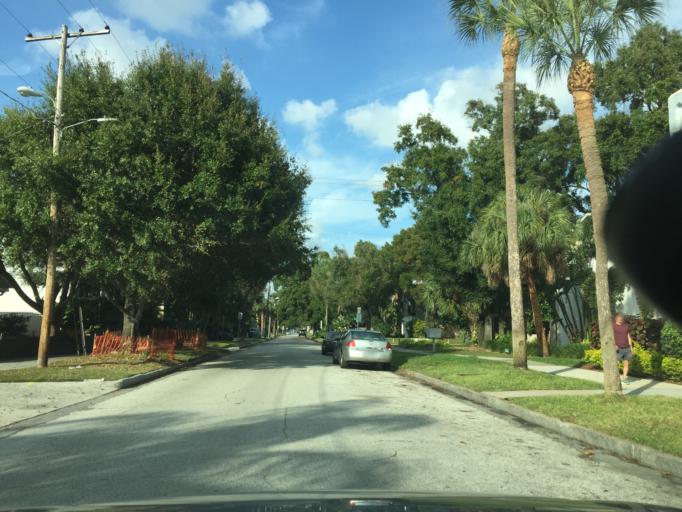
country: US
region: Florida
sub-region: Hillsborough County
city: Tampa
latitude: 27.9392
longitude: -82.4820
